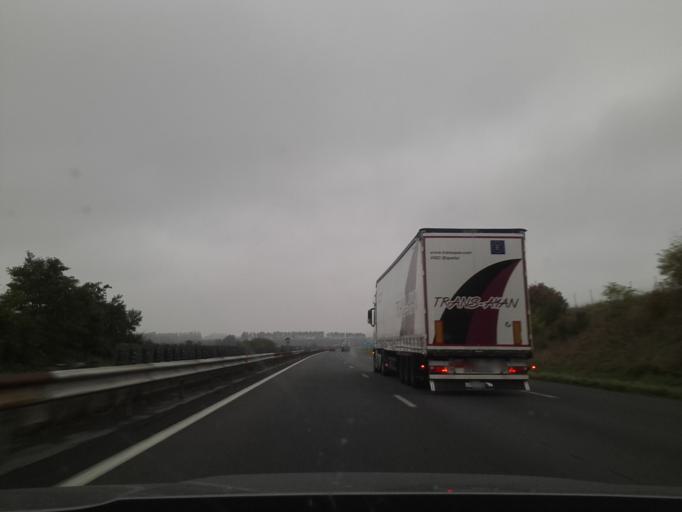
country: FR
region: Nord-Pas-de-Calais
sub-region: Departement du Nord
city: Raillencourt-Sainte-Olle
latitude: 50.1682
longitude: 3.1770
